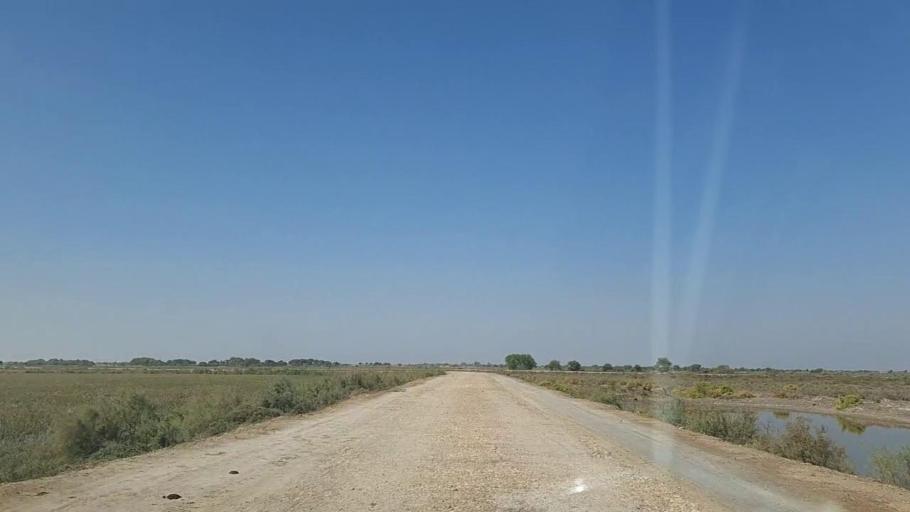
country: PK
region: Sindh
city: Chuhar Jamali
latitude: 24.4236
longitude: 68.0109
